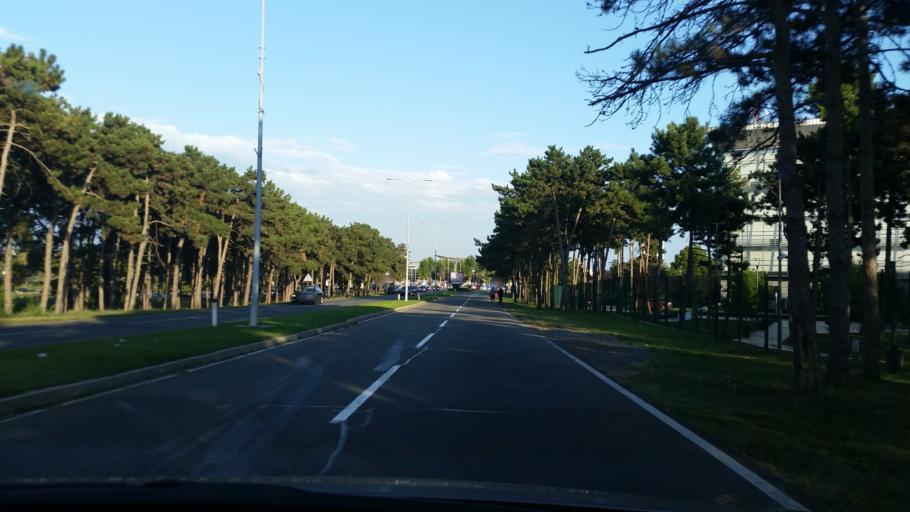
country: RS
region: Central Serbia
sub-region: Belgrade
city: Surcin
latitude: 44.8204
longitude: 20.2863
